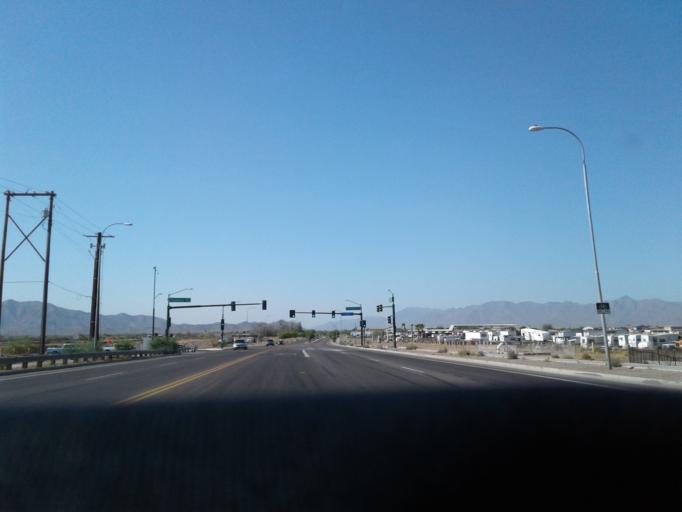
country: US
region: Arizona
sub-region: Maricopa County
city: Laveen
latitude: 33.4043
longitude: -112.1686
